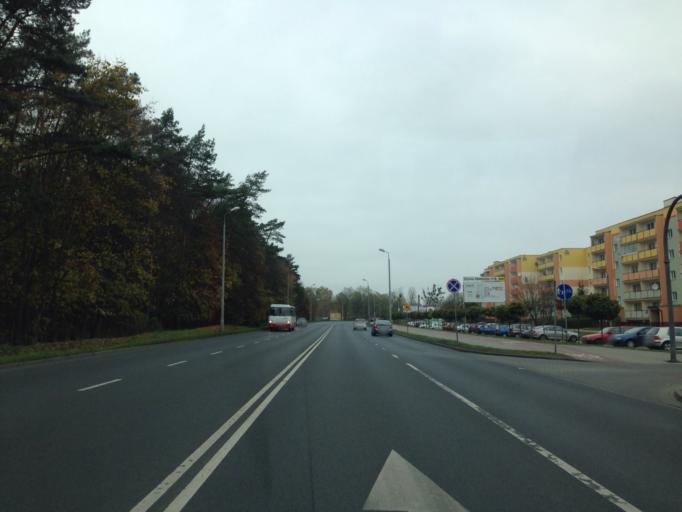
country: PL
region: Kujawsko-Pomorskie
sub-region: Grudziadz
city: Grudziadz
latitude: 53.4626
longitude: 18.7681
